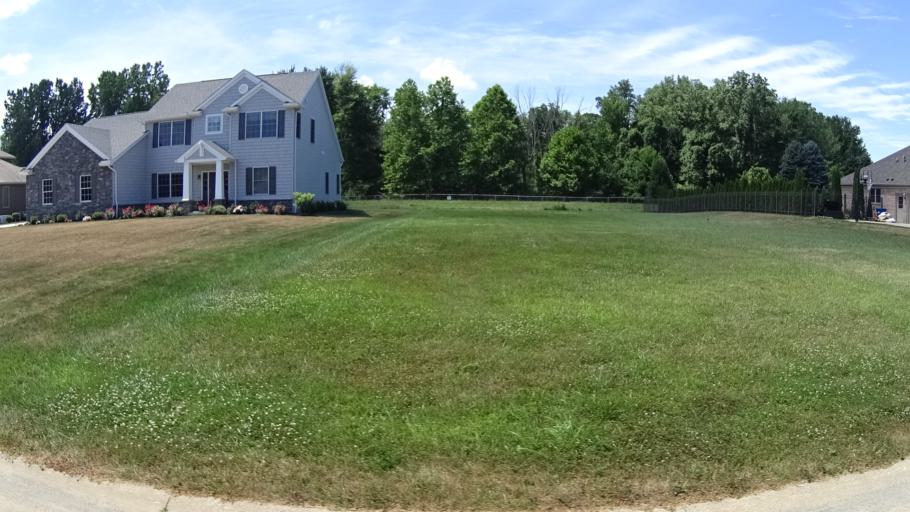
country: US
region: Ohio
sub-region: Erie County
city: Sandusky
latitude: 41.3943
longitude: -82.6755
